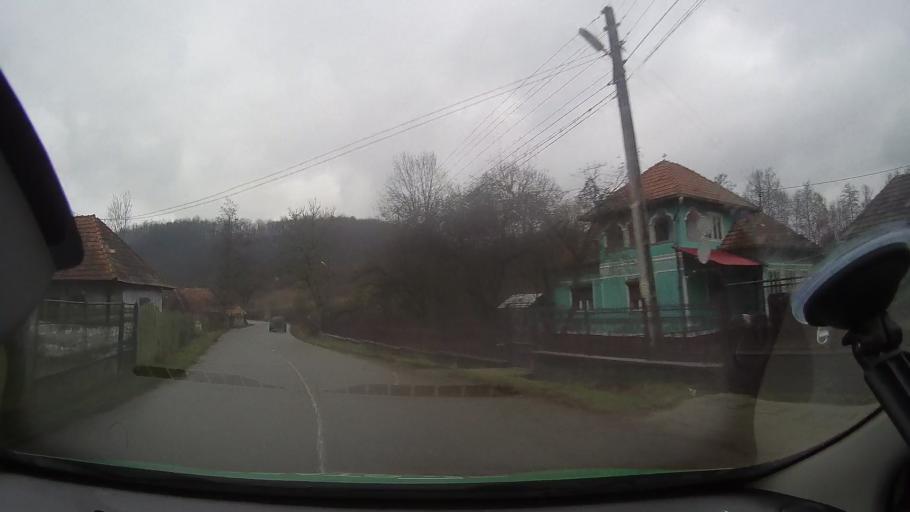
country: RO
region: Hunedoara
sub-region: Comuna Tomesti
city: Tomesti
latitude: 46.1991
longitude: 22.6507
